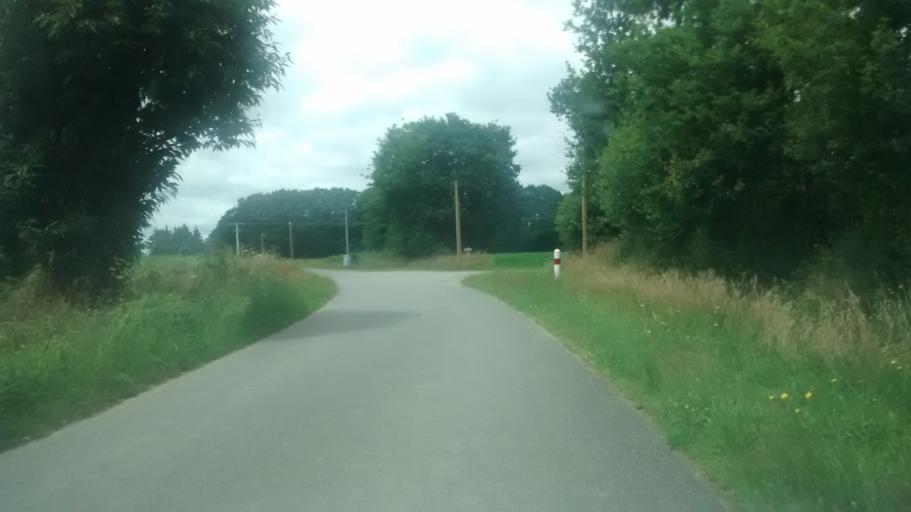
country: FR
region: Brittany
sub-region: Departement du Morbihan
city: Malestroit
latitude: 47.7873
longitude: -2.4304
